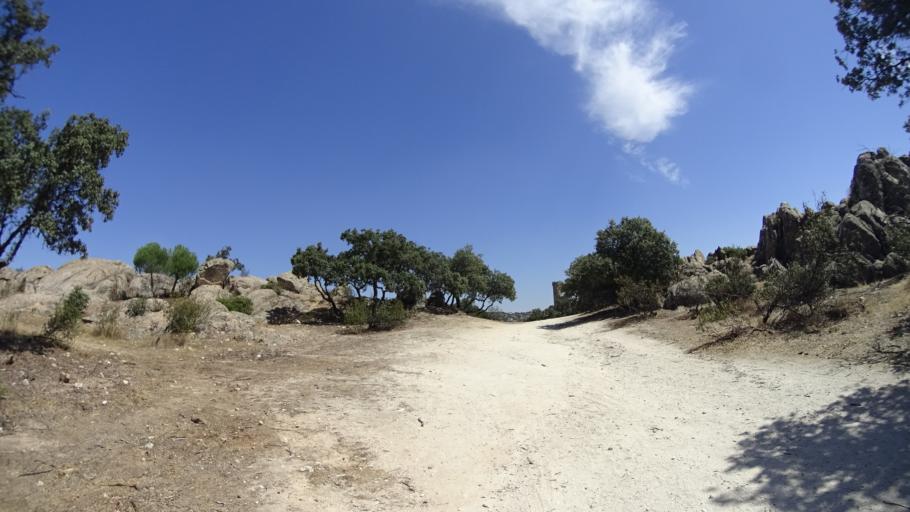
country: ES
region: Madrid
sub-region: Provincia de Madrid
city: Torrelodones
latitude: 40.5726
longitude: -3.9340
